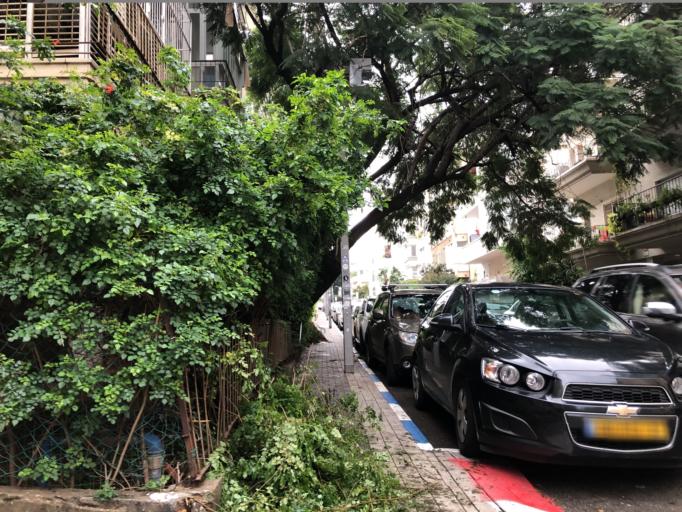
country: IL
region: Tel Aviv
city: Tel Aviv
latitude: 32.0716
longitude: 34.7750
